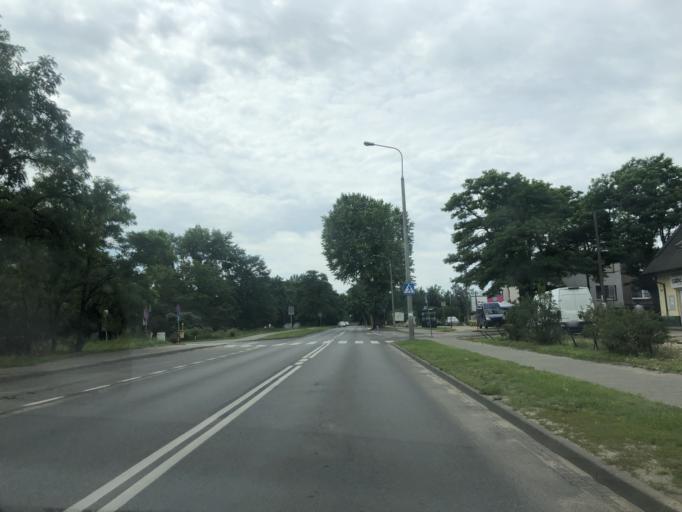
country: PL
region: Greater Poland Voivodeship
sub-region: Powiat poznanski
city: Lubon
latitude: 52.3598
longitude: 16.8876
